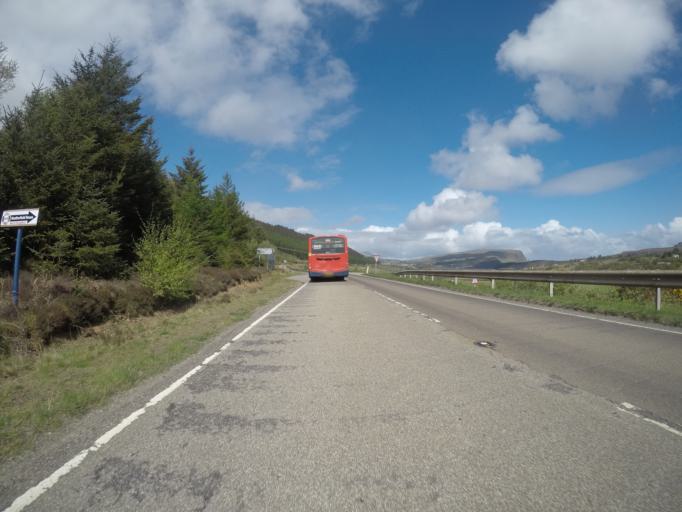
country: GB
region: Scotland
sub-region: Highland
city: Portree
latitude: 57.3871
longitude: -6.2040
